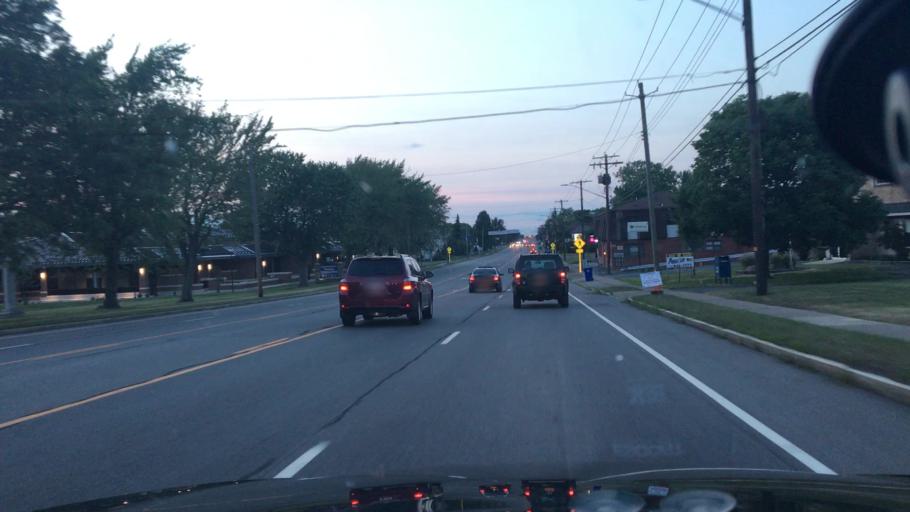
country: US
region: New York
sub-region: Erie County
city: West Seneca
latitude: 42.8343
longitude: -78.7538
